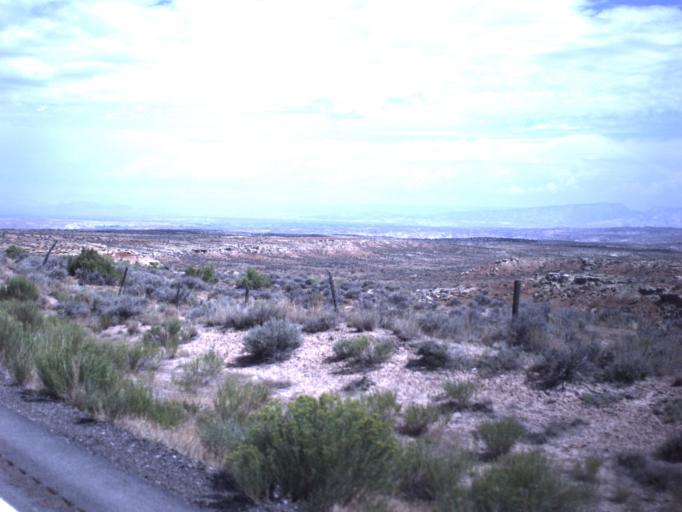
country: US
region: Utah
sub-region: Uintah County
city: Naples
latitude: 40.2176
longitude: -109.3842
